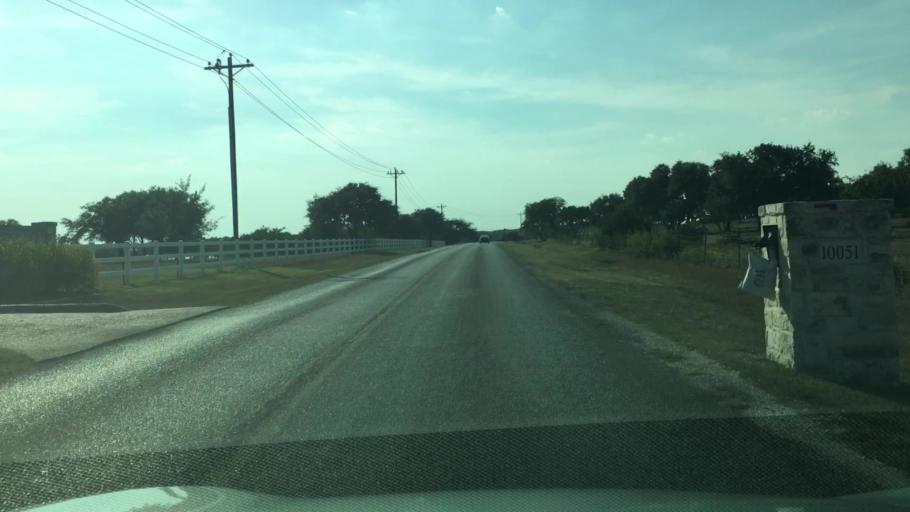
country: US
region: Texas
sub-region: Hays County
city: Dripping Springs
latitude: 30.1491
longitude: -97.9909
